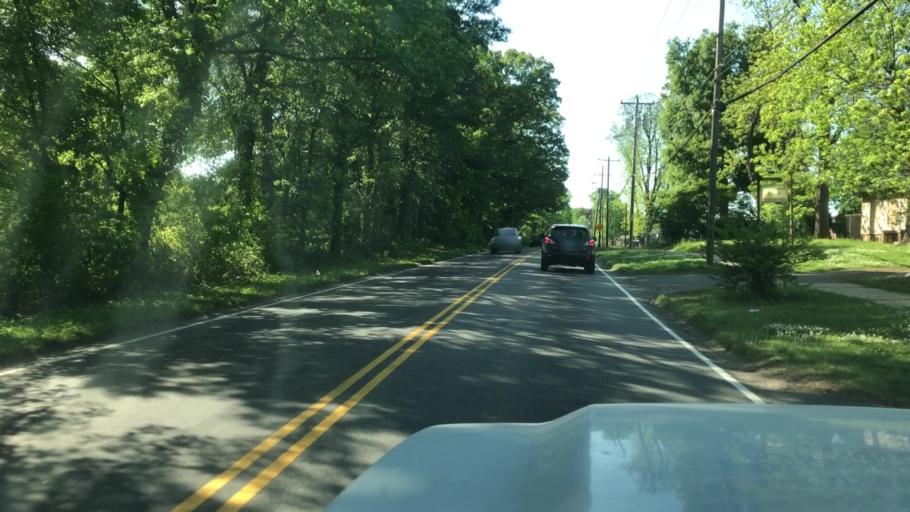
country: US
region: North Carolina
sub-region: Mecklenburg County
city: Charlotte
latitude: 35.2771
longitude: -80.8972
